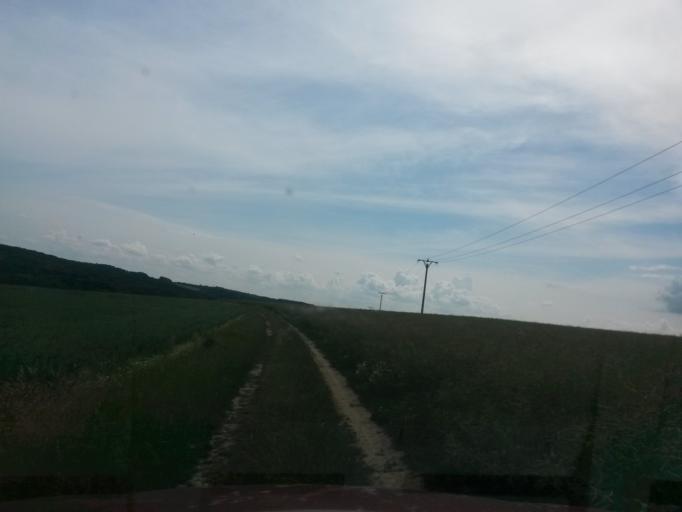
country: SK
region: Kosicky
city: Moldava nad Bodvou
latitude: 48.6581
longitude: 21.1097
